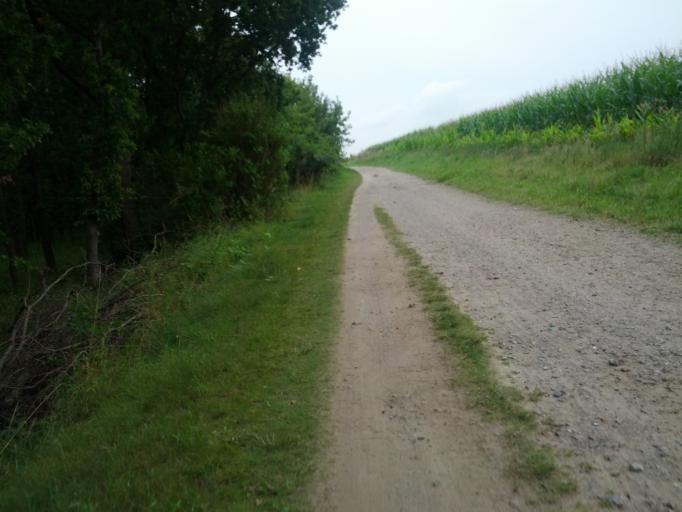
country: DE
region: Mecklenburg-Vorpommern
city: Ostseebad Kuhlungsborn
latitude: 54.1439
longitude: 11.8170
